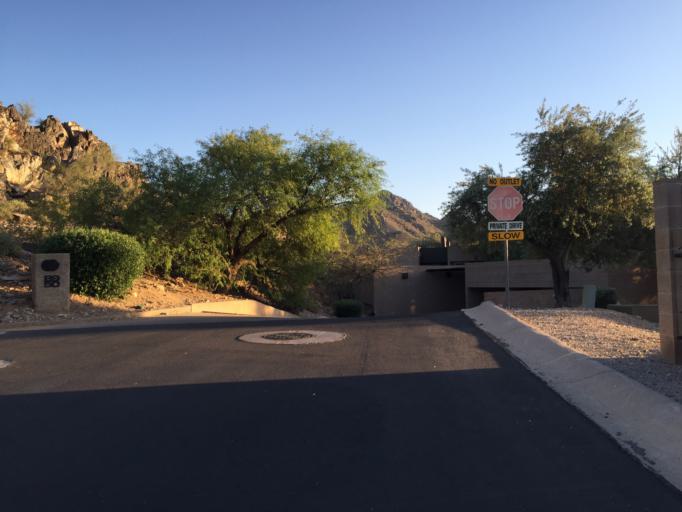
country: US
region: Arizona
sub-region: Maricopa County
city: Paradise Valley
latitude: 33.5679
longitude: -112.0160
